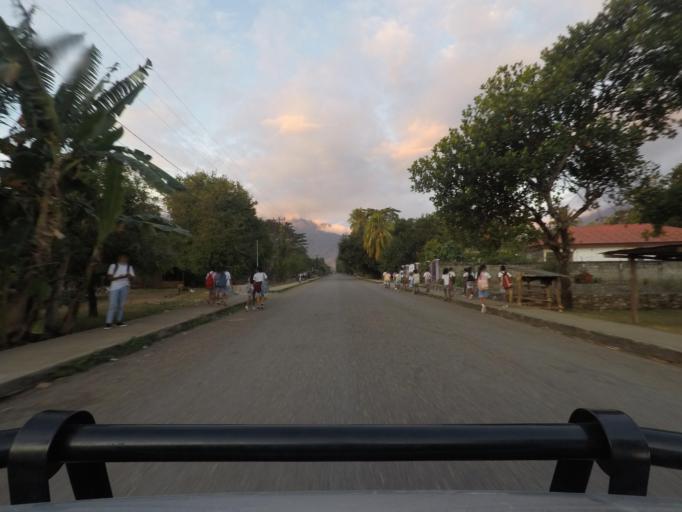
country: TL
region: Bobonaro
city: Maliana
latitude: -8.9903
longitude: 125.2033
